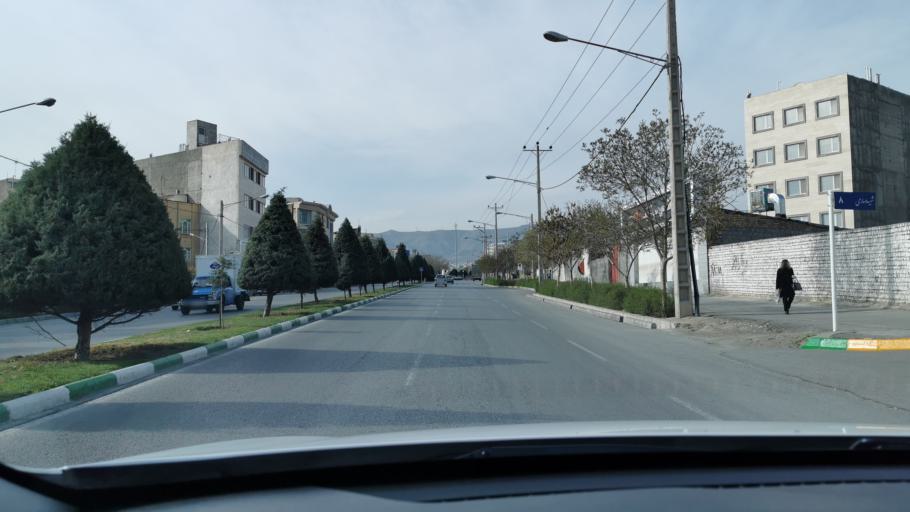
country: IR
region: Razavi Khorasan
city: Mashhad
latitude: 36.3070
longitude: 59.5139
